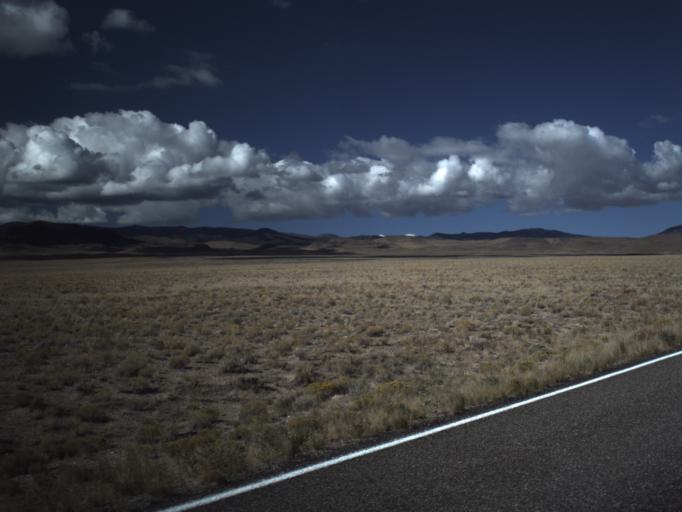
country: US
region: Utah
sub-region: Beaver County
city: Milford
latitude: 38.5719
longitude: -113.7892
